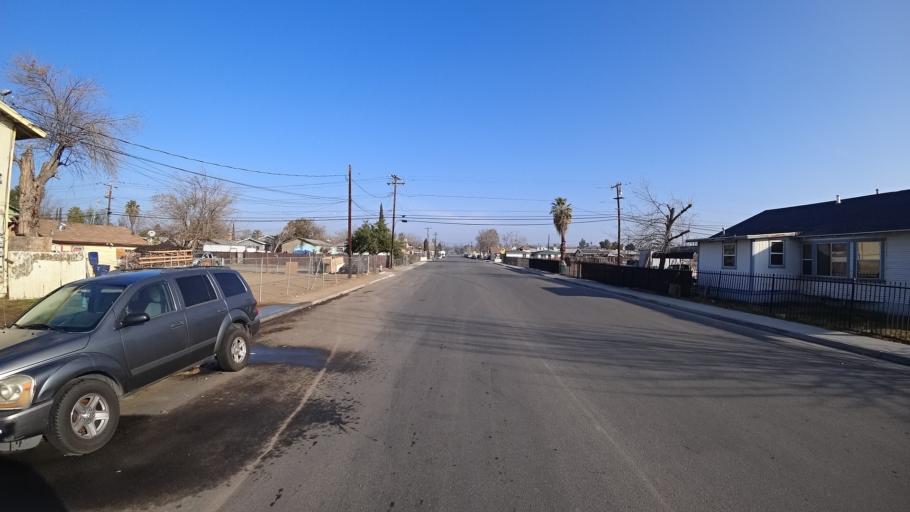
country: US
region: California
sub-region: Kern County
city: Bakersfield
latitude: 35.3757
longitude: -118.9783
